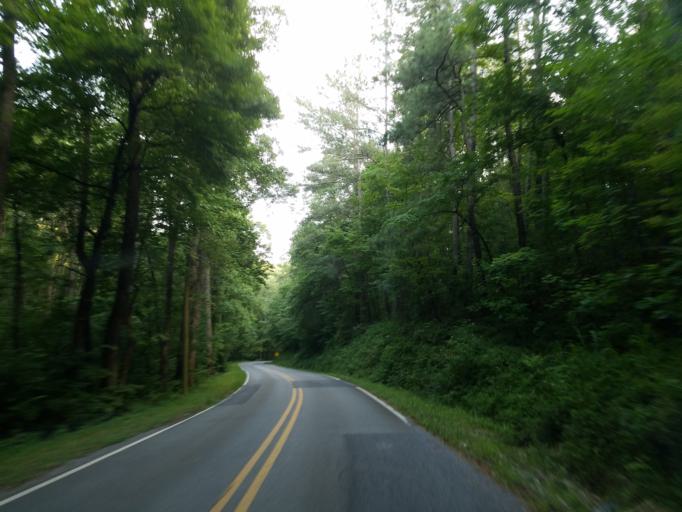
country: US
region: Georgia
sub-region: Pickens County
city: Jasper
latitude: 34.4855
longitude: -84.4178
